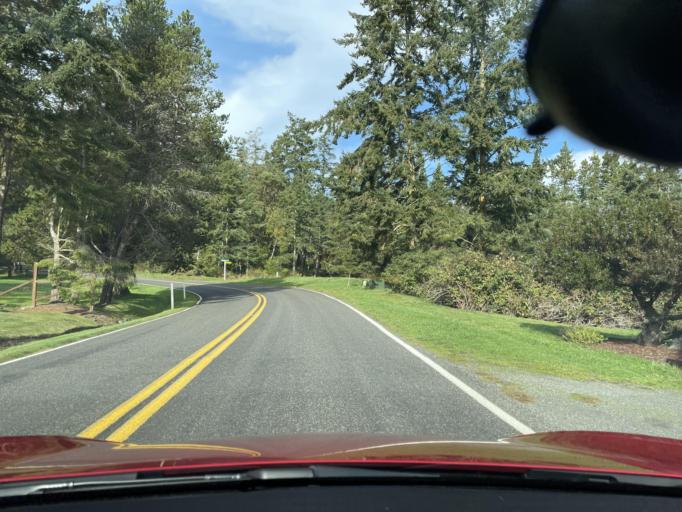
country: US
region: Washington
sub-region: San Juan County
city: Friday Harbor
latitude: 48.5283
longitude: -122.9815
